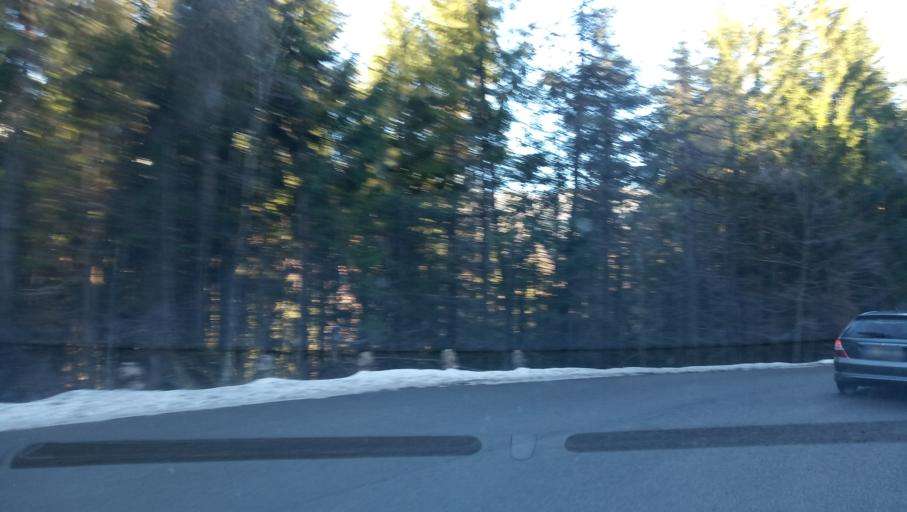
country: RO
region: Brasov
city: Crivina
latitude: 45.4812
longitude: 25.9160
